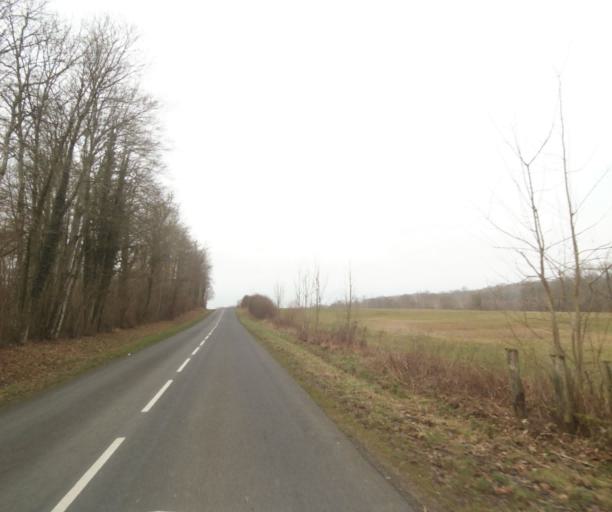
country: FR
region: Champagne-Ardenne
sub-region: Departement de la Marne
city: Pargny-sur-Saulx
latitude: 48.7394
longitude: 4.8711
